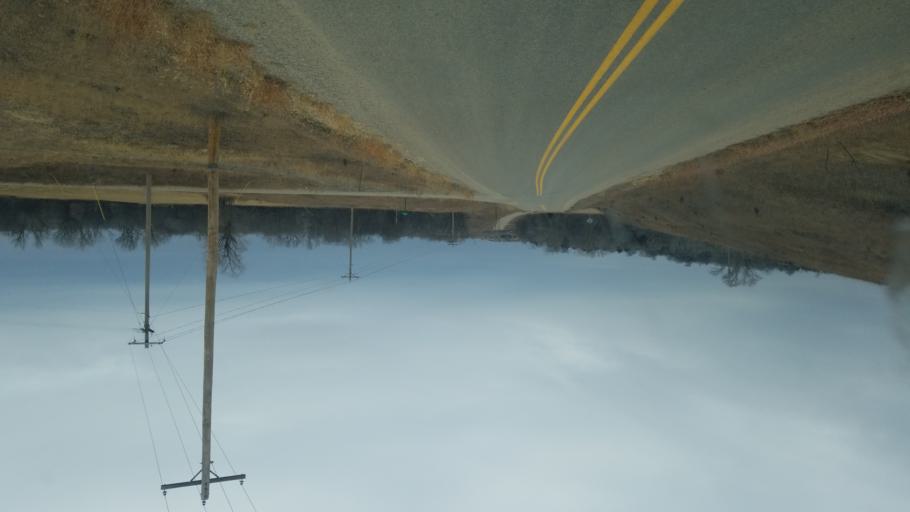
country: US
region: Nebraska
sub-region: Knox County
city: Center
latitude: 42.6683
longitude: -97.8879
